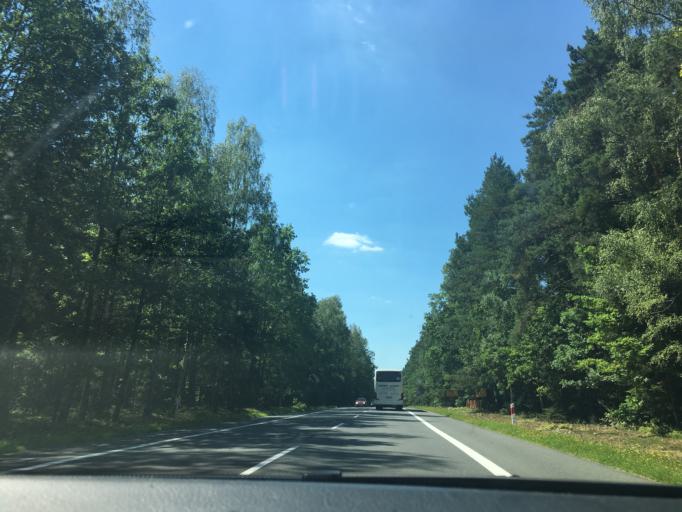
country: PL
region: Subcarpathian Voivodeship
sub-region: Powiat nizanski
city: Zarzecze
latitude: 50.5548
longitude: 22.2356
